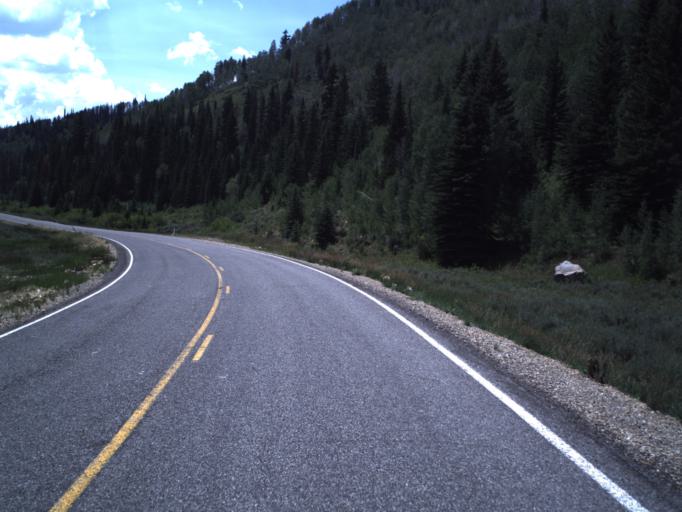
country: US
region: Utah
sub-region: Sanpete County
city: Fairview
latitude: 39.6637
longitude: -111.1556
